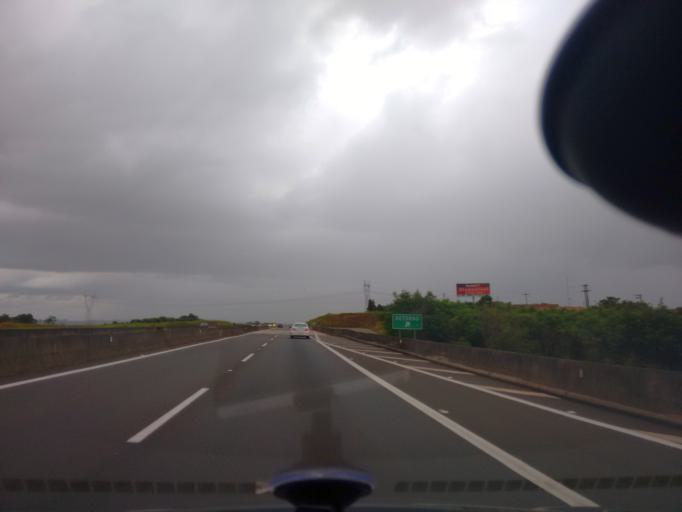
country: BR
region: Sao Paulo
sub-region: Santa Barbara D'Oeste
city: Santa Barbara d'Oeste
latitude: -22.7045
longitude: -47.4561
